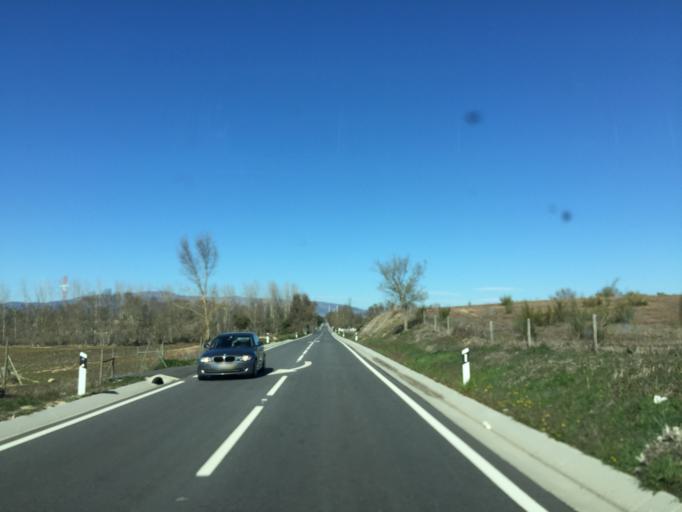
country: PT
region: Guarda
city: Alcains
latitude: 39.9670
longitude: -7.4539
